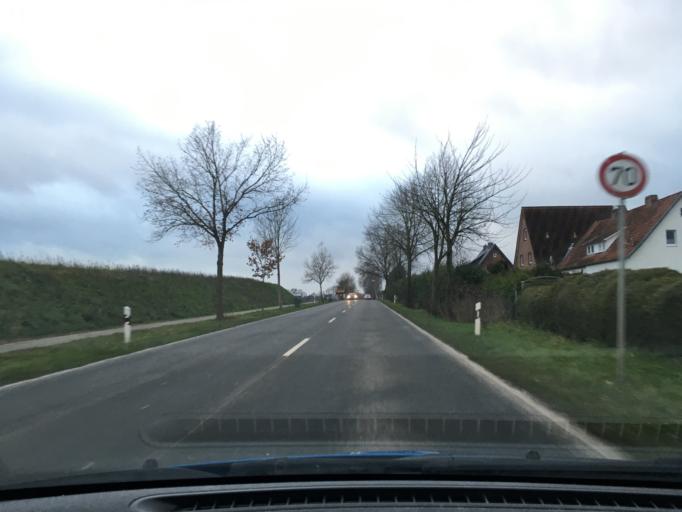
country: DE
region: Lower Saxony
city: Hermannsburg
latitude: 52.8760
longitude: 10.1076
